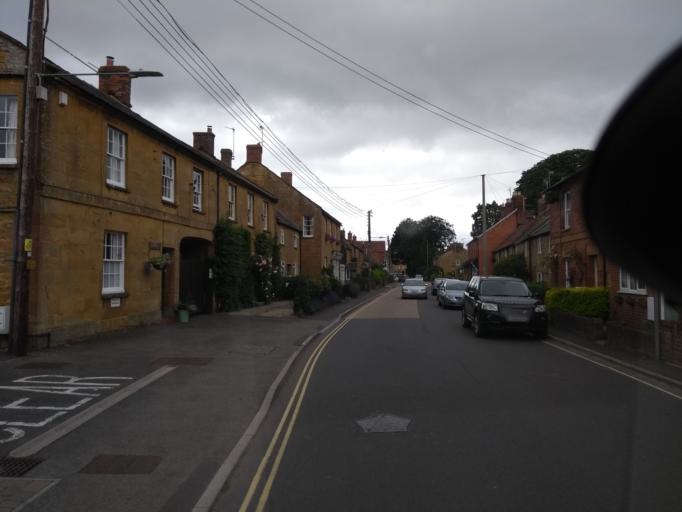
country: GB
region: England
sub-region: Somerset
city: Martock
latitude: 50.9733
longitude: -2.7669
